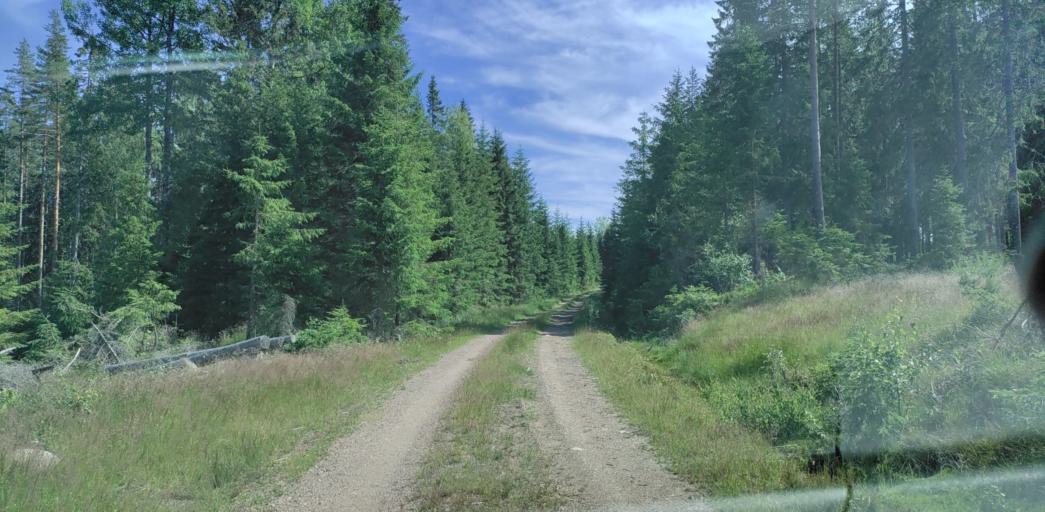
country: SE
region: Vaermland
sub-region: Hagfors Kommun
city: Ekshaerad
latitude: 60.0930
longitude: 13.3753
